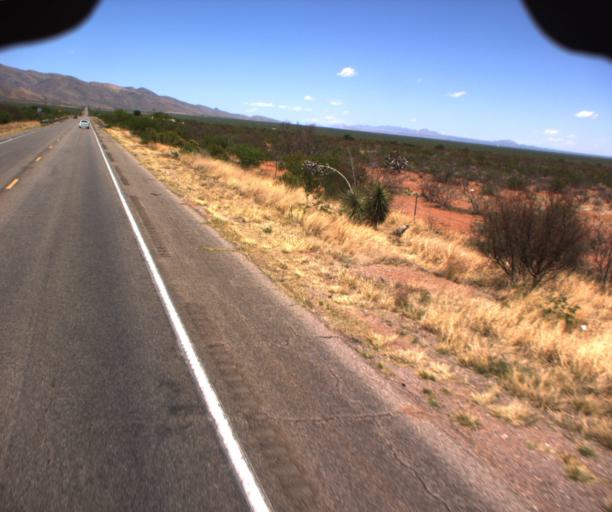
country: US
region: Arizona
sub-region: Cochise County
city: Bisbee
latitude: 31.3975
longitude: -109.7720
